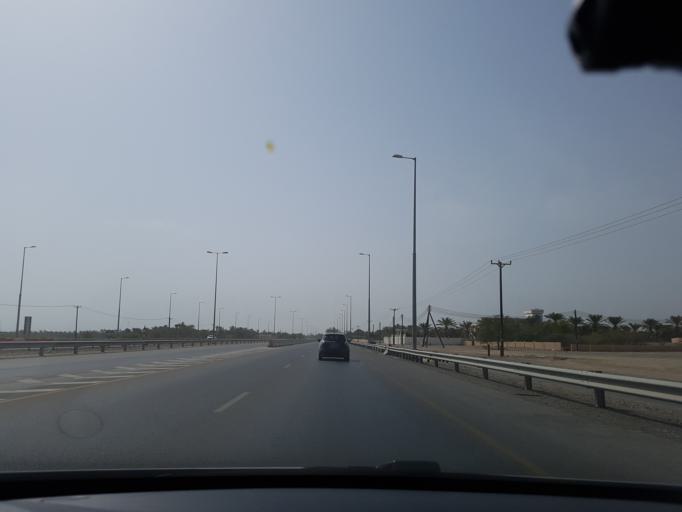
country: OM
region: Al Batinah
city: Al Khaburah
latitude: 23.9620
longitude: 57.0978
